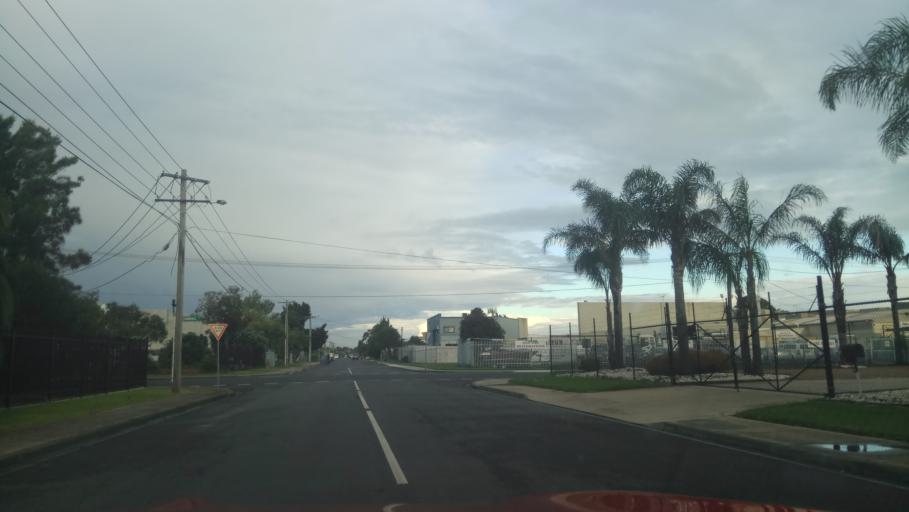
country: AU
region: Victoria
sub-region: Hobsons Bay
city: Williamstown North
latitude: -37.8508
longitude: 144.8625
